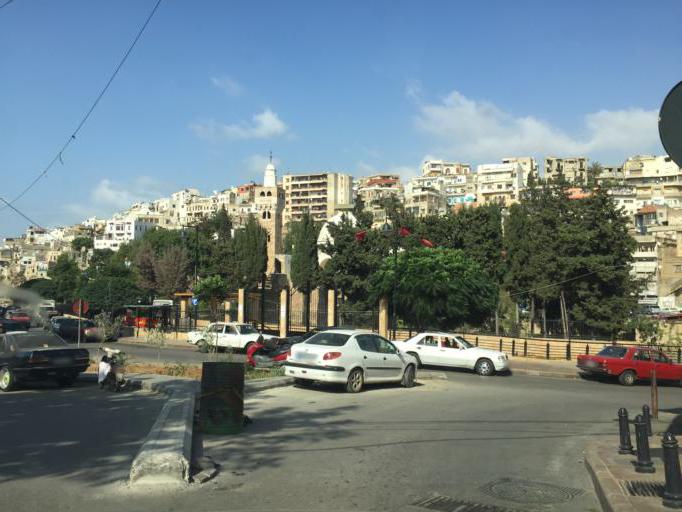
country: LB
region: Liban-Nord
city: Tripoli
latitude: 34.4354
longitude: 35.8455
